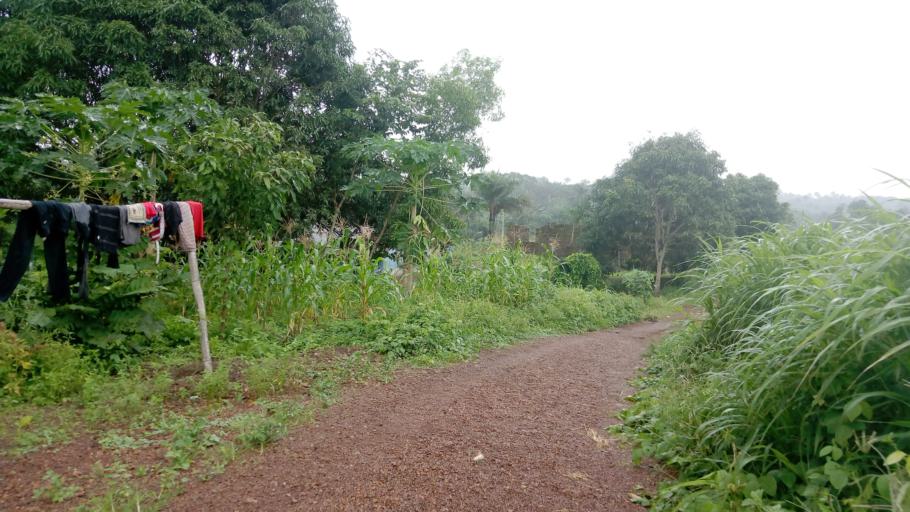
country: SL
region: Southern Province
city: Rotifunk
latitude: 8.4826
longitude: -12.7592
